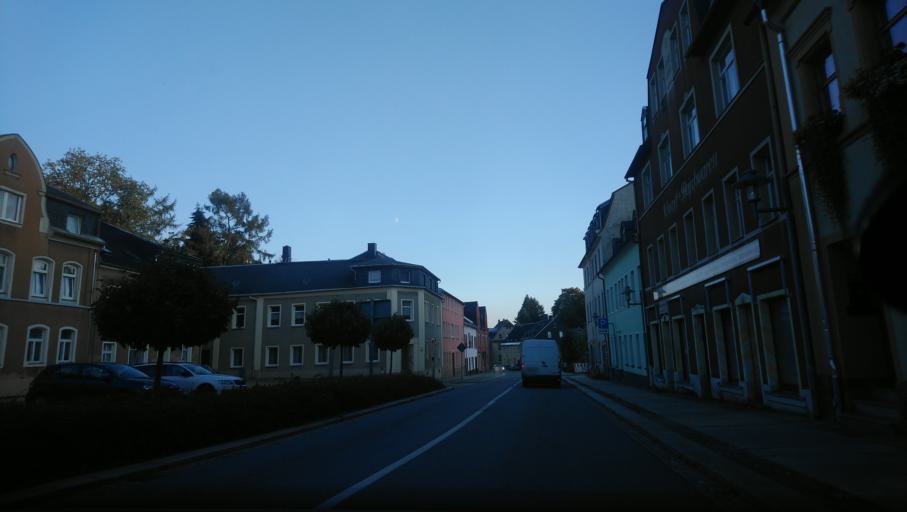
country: DE
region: Saxony
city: Geyer
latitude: 50.6234
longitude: 12.9235
